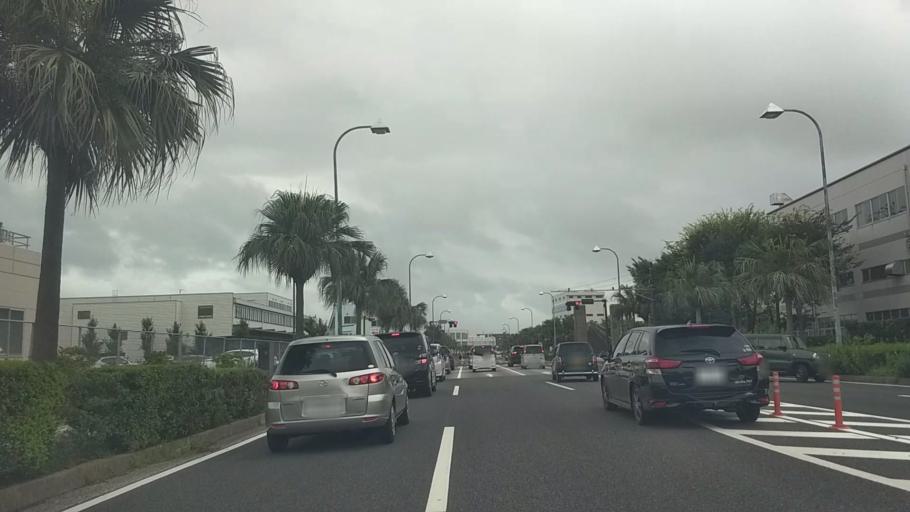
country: JP
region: Kanagawa
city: Yokosuka
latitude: 35.2702
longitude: 139.6857
